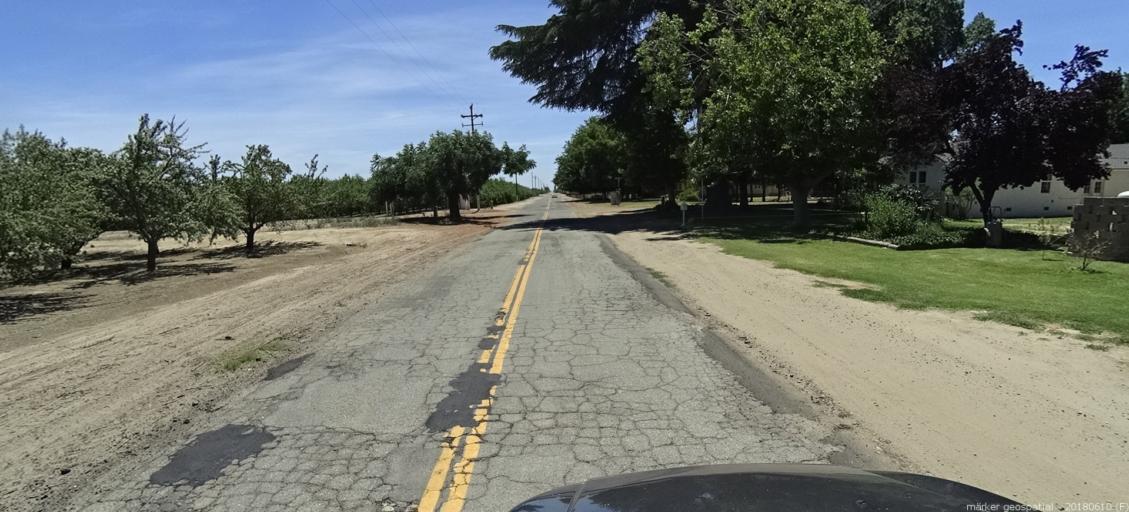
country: US
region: California
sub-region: Madera County
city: Chowchilla
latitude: 37.0768
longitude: -120.2927
